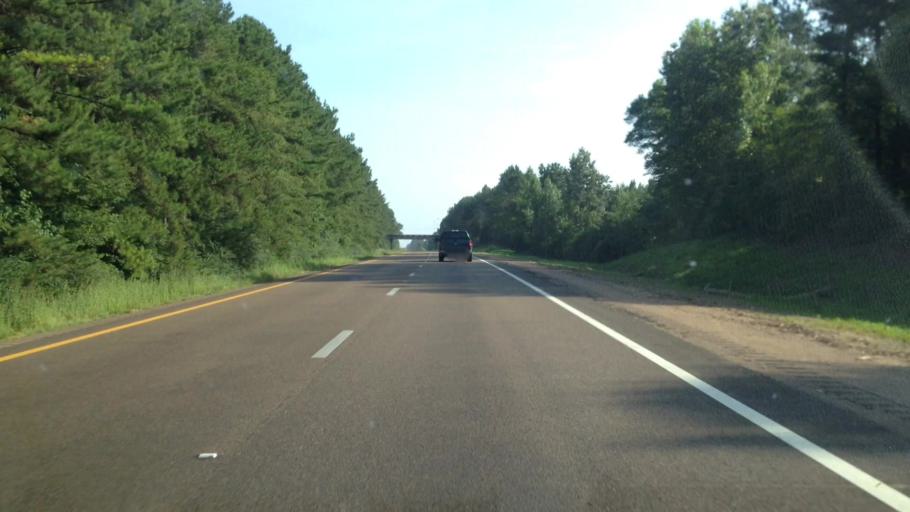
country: US
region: Mississippi
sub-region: Lincoln County
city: Brookhaven
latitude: 31.4463
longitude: -90.4793
